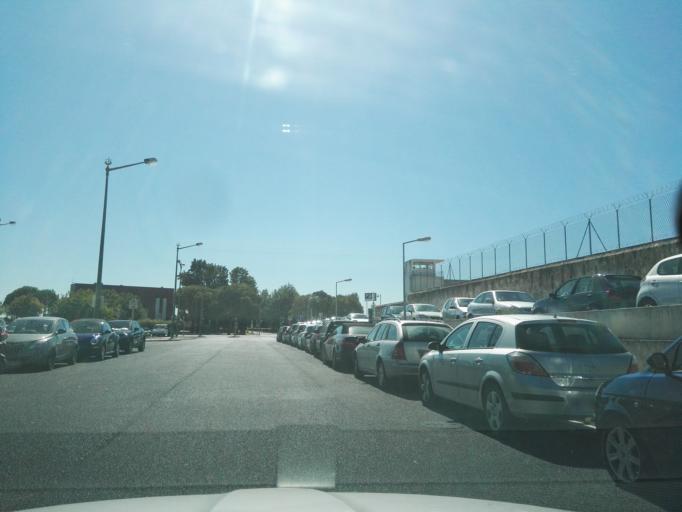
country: PT
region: Lisbon
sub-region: Lisbon
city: Lisbon
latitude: 38.7316
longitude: -9.1574
